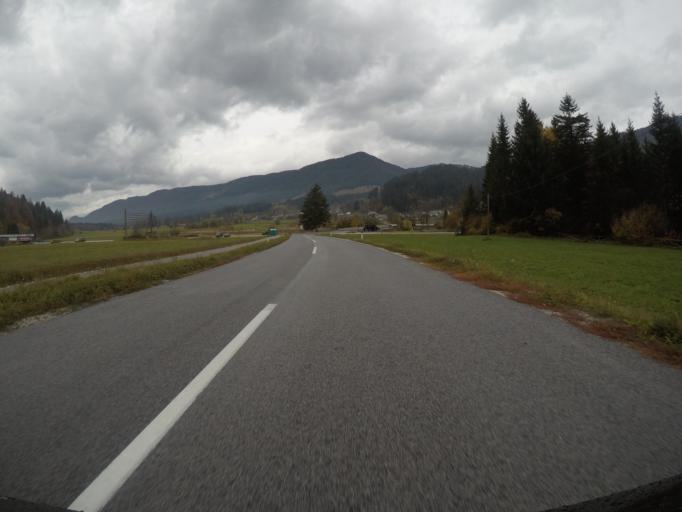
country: AT
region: Carinthia
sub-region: Politischer Bezirk Villach Land
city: Arnoldstein
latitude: 46.4907
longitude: 13.7232
